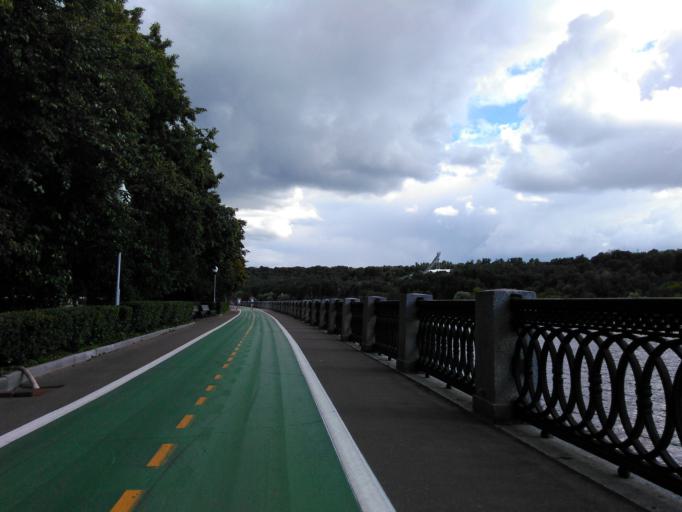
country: RU
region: Moscow
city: Vorob'yovo
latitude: 55.7179
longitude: 37.5435
